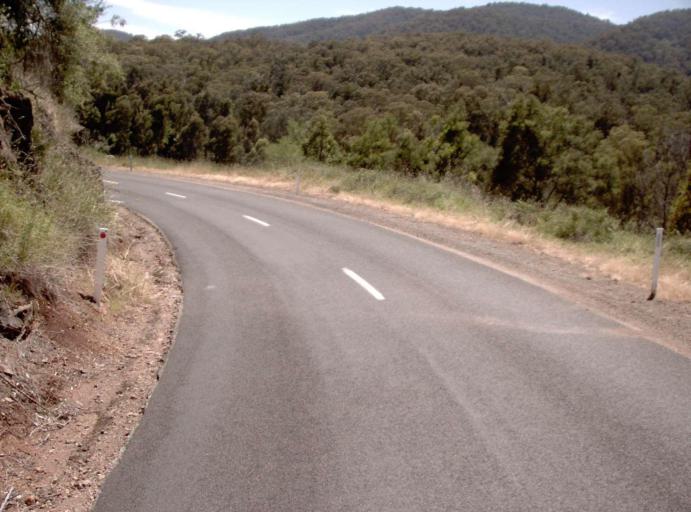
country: AU
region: Victoria
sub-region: East Gippsland
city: Lakes Entrance
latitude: -37.4068
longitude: 148.2112
